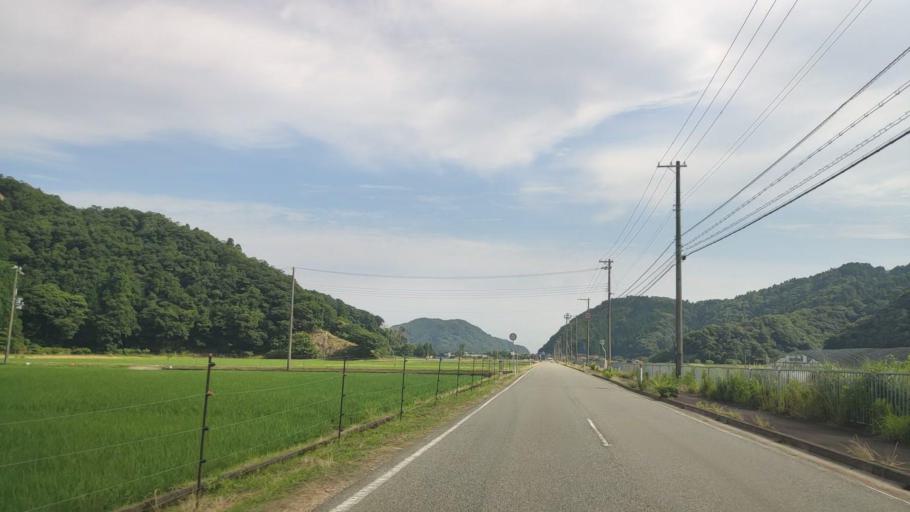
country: JP
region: Hyogo
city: Toyooka
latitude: 35.6270
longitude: 134.8411
